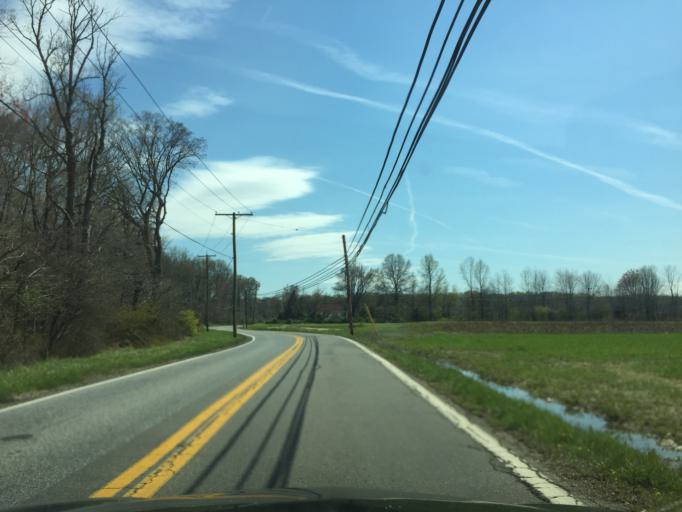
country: US
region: Maryland
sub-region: Baltimore County
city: Edgemere
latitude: 39.2786
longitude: -76.4270
